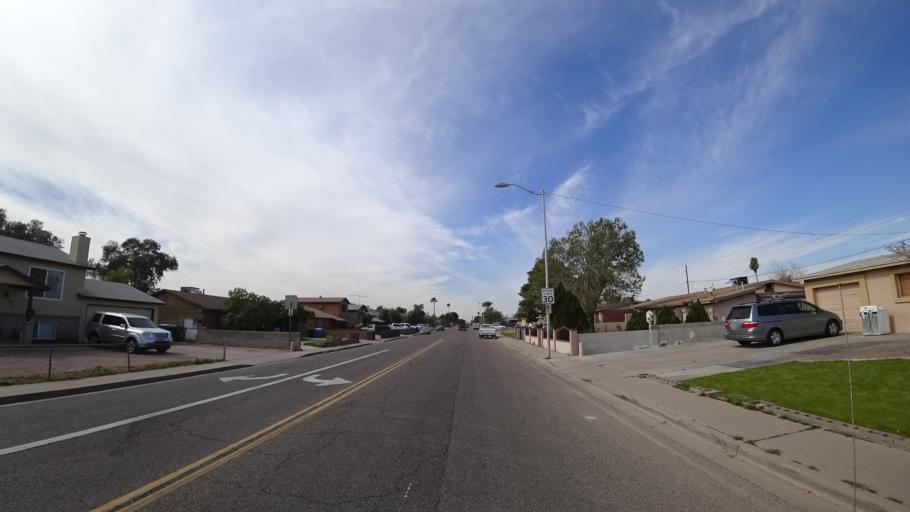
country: US
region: Arizona
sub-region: Maricopa County
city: Tolleson
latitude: 33.4875
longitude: -112.2212
